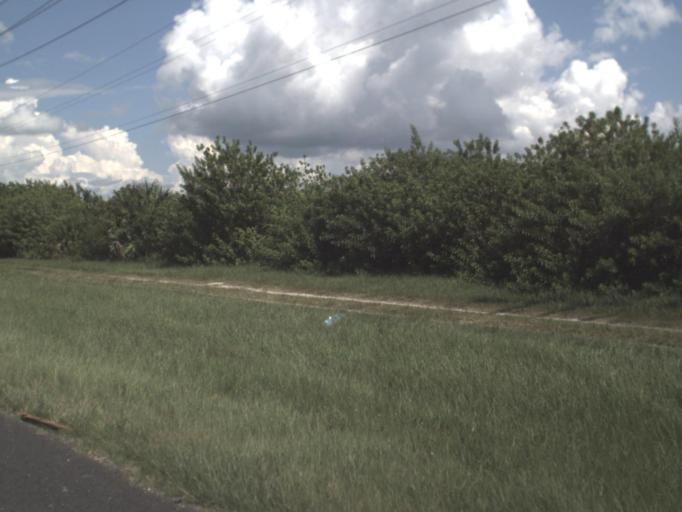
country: US
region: Florida
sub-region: Hillsborough County
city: Tampa
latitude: 27.9304
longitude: -82.4272
